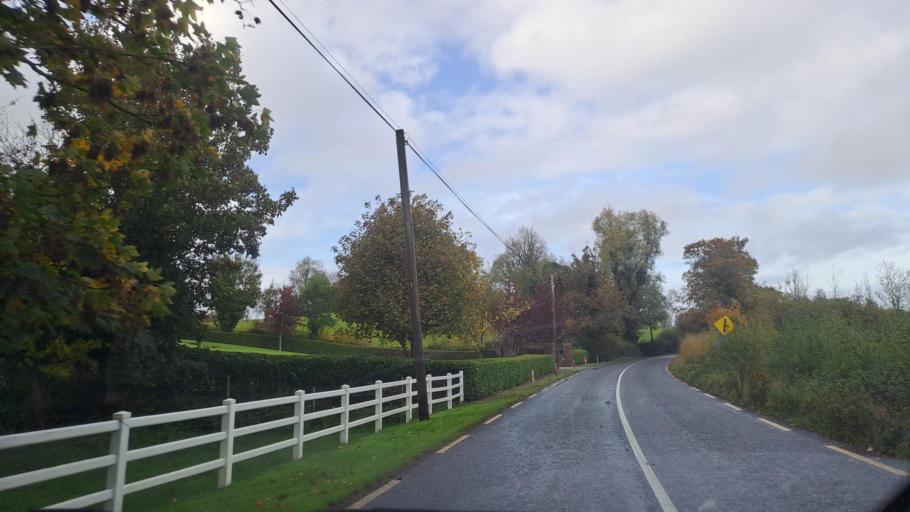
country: IE
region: Ulster
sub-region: County Monaghan
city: Carrickmacross
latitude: 53.9129
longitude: -6.7077
